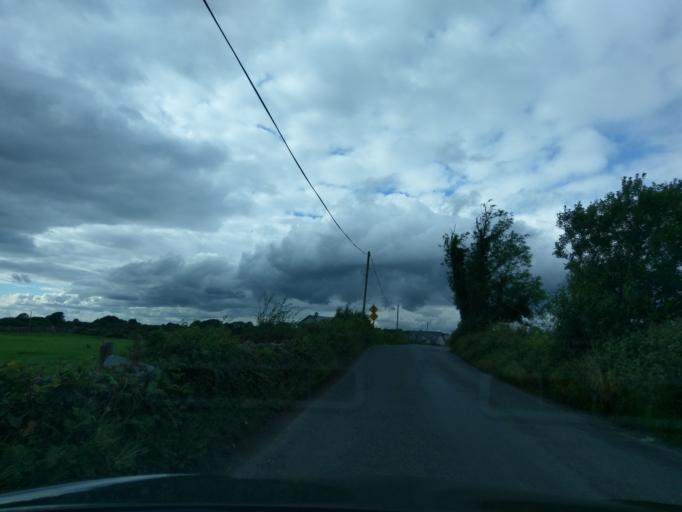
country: IE
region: Connaught
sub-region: County Galway
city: Athenry
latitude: 53.2482
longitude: -8.7484
